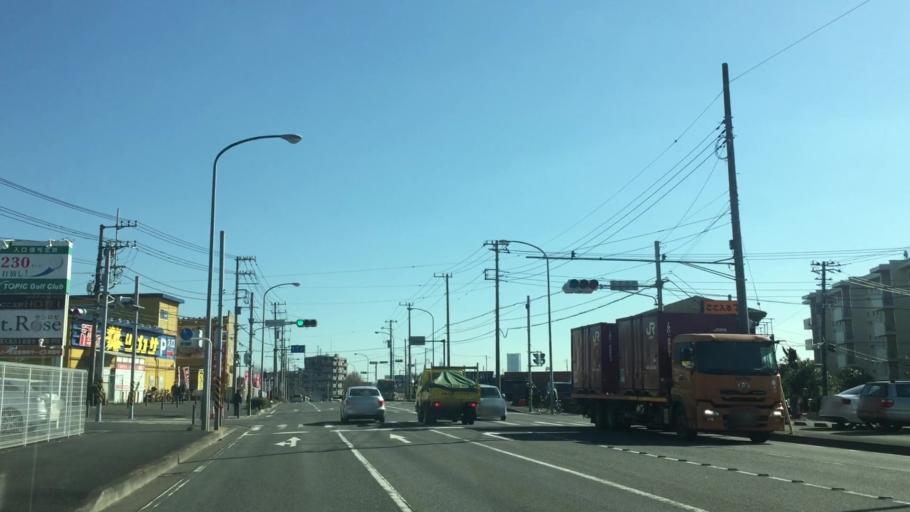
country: JP
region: Kanagawa
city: Yokohama
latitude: 35.4835
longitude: 139.5969
